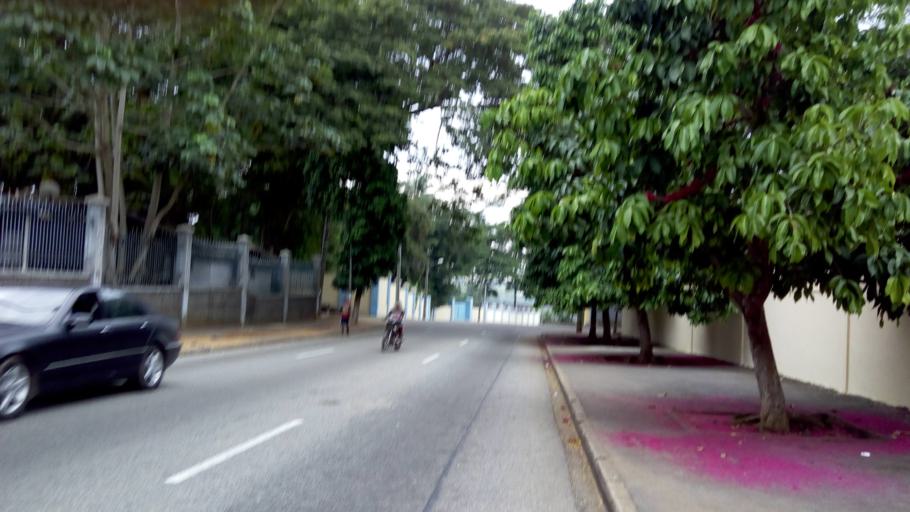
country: CI
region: Lagunes
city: Abidjan
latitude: 5.3210
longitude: -4.0213
